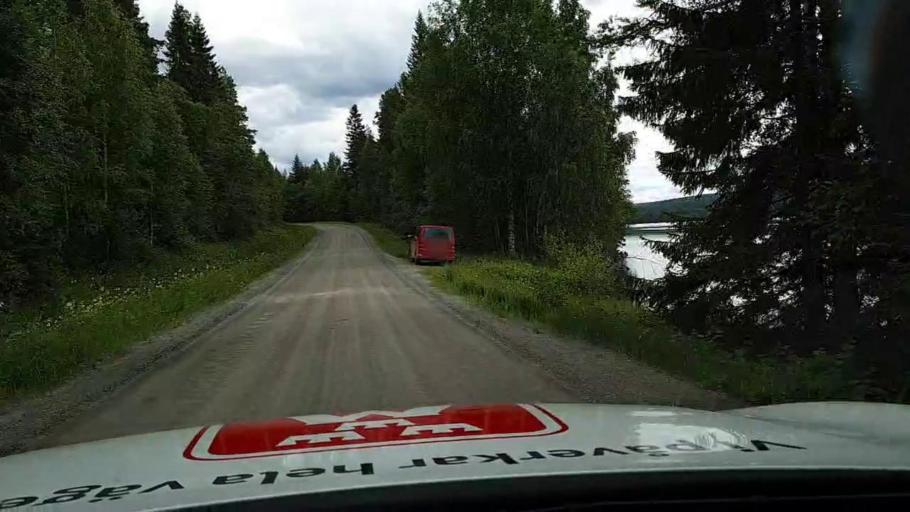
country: SE
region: Jaemtland
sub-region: Braecke Kommun
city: Braecke
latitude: 63.2124
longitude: 15.3720
